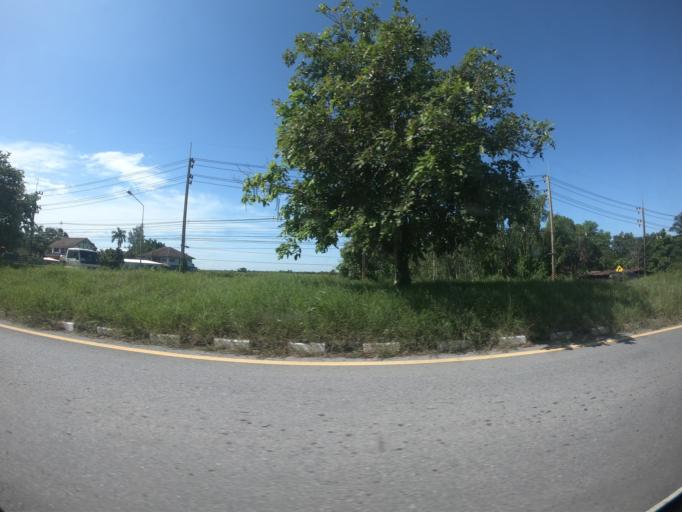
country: TH
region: Nakhon Nayok
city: Ban Na
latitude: 14.2397
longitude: 101.1298
